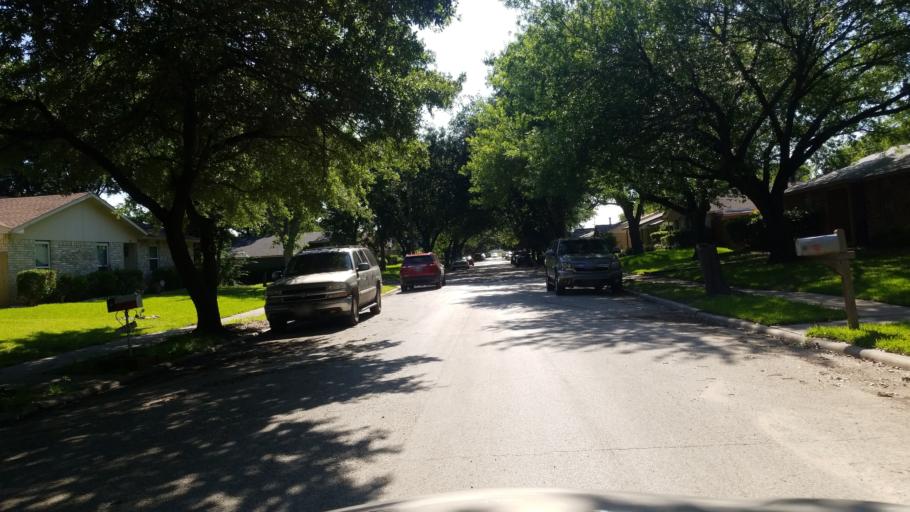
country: US
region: Texas
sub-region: Dallas County
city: Grand Prairie
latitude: 32.6850
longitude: -97.0149
